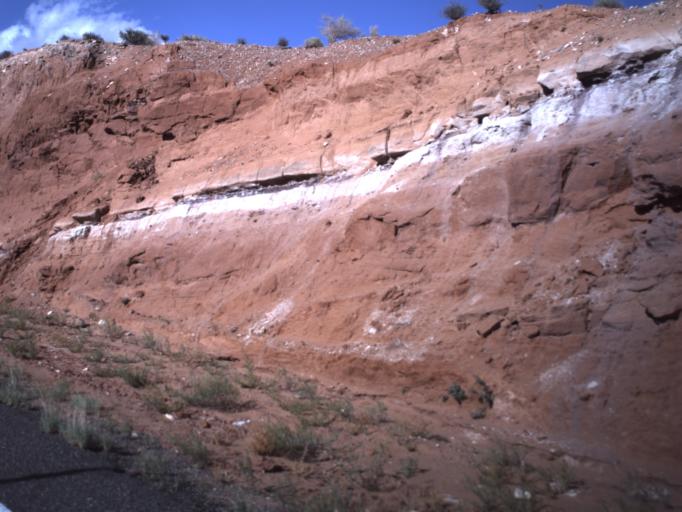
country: US
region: Utah
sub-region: Wayne County
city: Loa
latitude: 38.0739
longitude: -110.6085
